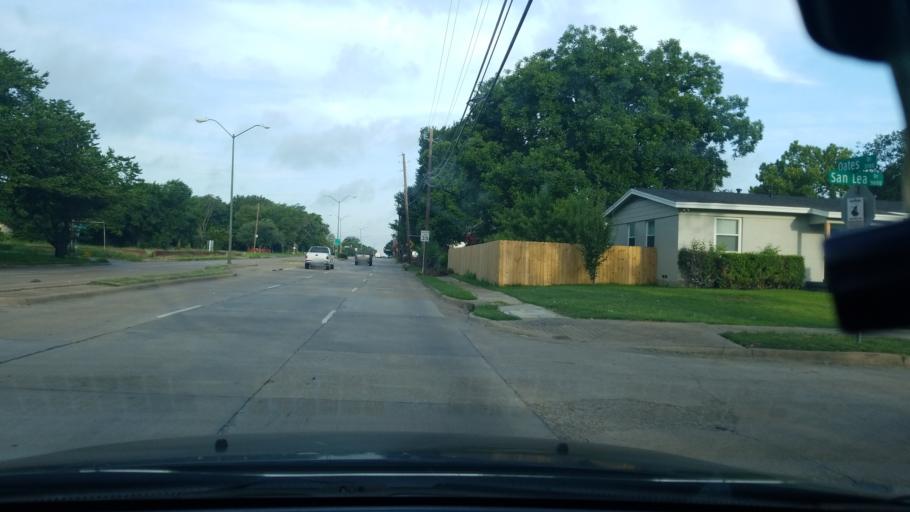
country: US
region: Texas
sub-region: Dallas County
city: Mesquite
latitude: 32.8216
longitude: -96.6616
